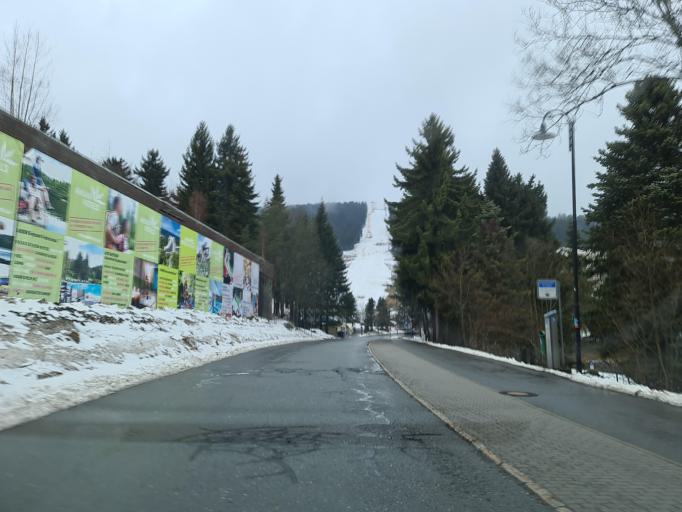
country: DE
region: Saxony
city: Kurort Oberwiesenthal
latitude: 50.4229
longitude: 12.9701
